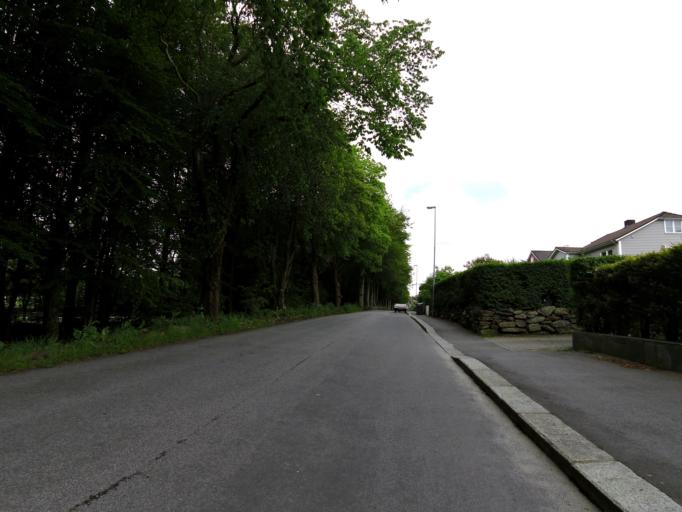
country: NO
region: Rogaland
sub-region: Stavanger
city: Stavanger
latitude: 58.9609
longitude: 5.7085
